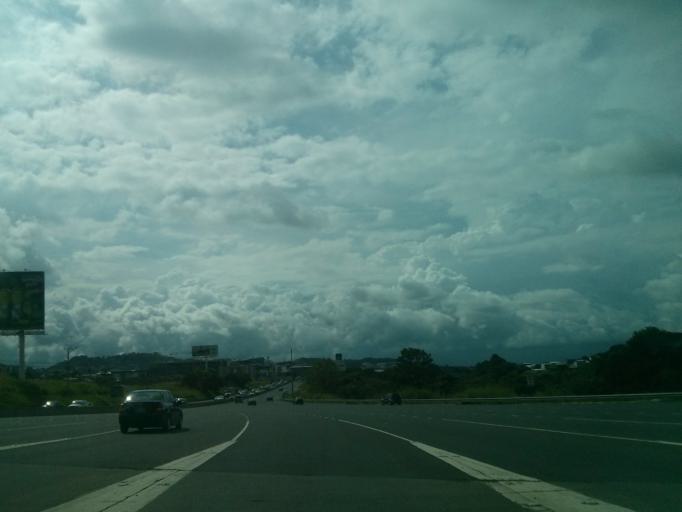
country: CR
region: San Jose
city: San Rafael
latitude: 9.9379
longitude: -84.1361
